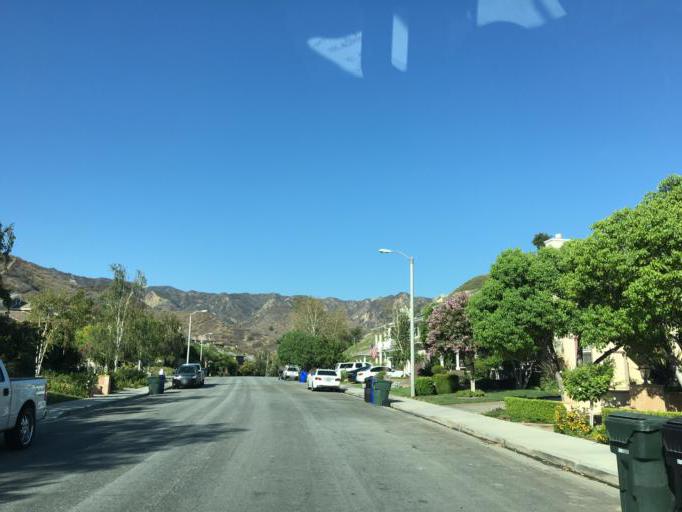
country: US
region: California
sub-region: Los Angeles County
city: Santa Clarita
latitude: 34.3767
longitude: -118.5837
